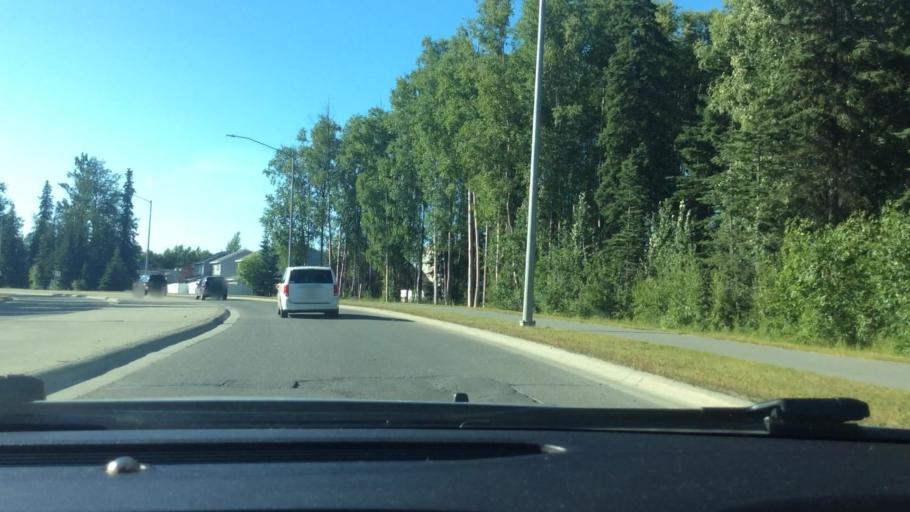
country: US
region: Alaska
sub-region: Anchorage Municipality
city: Anchorage
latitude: 61.2324
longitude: -149.7689
